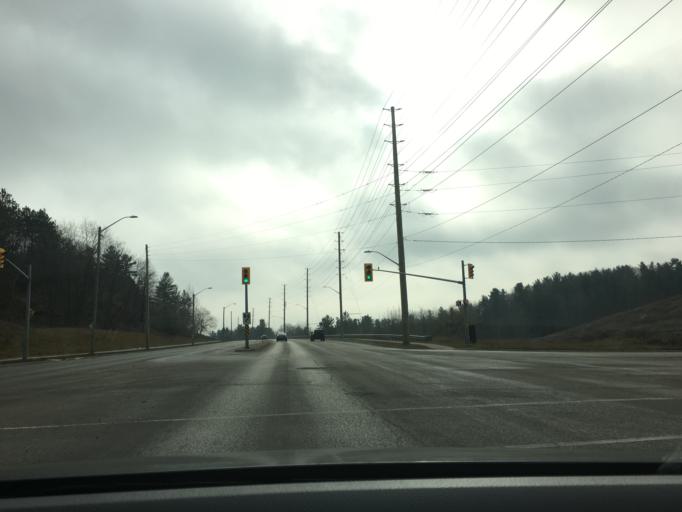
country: CA
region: Ontario
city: Barrie
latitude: 44.3865
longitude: -79.7294
